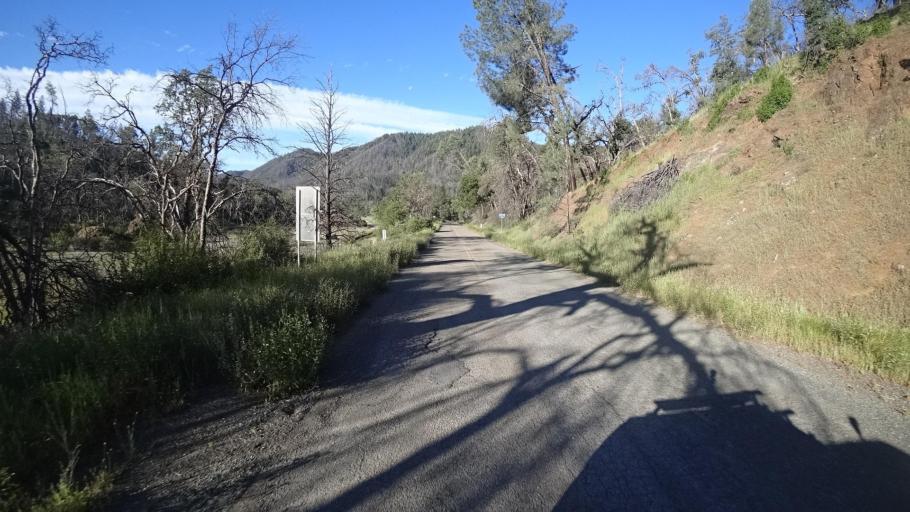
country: US
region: California
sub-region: Lake County
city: Upper Lake
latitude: 39.2558
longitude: -122.9486
